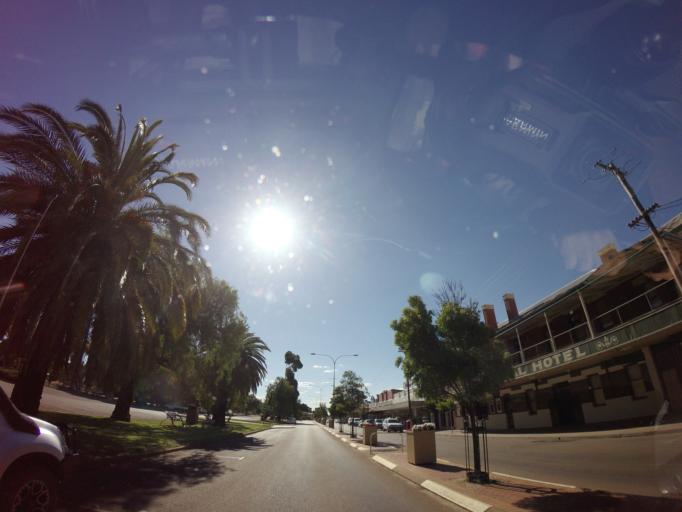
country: AU
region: Western Australia
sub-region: Merredin
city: Merredin
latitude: -31.4820
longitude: 118.2776
